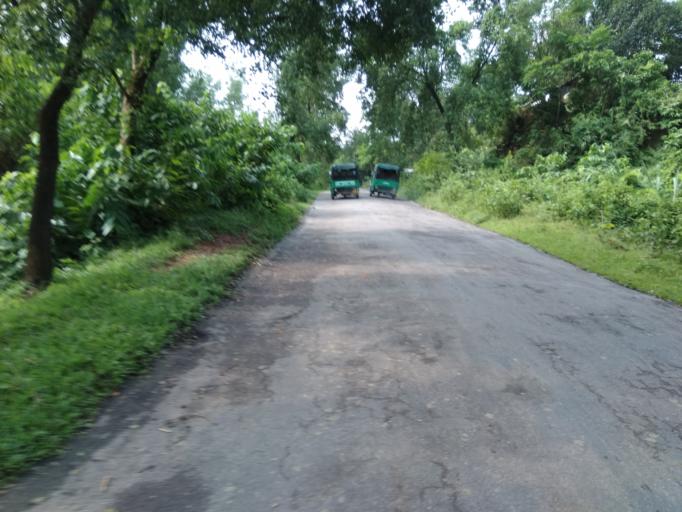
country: BD
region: Chittagong
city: Khagrachhari
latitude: 23.0045
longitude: 92.0112
